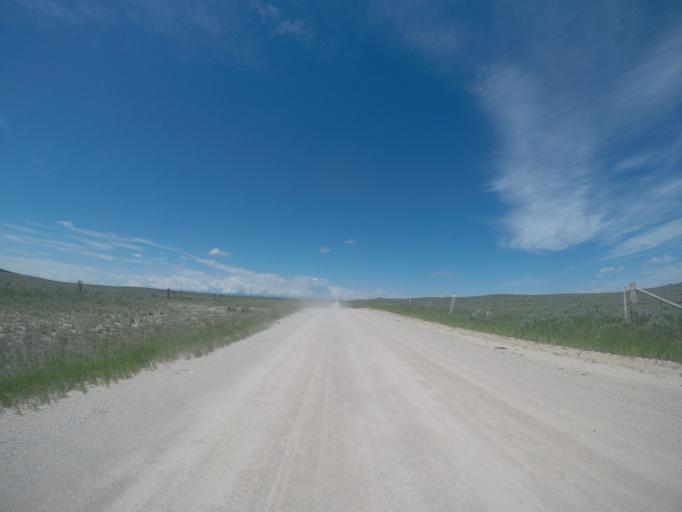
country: US
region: Wyoming
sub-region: Park County
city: Powell
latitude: 45.2050
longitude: -108.7396
